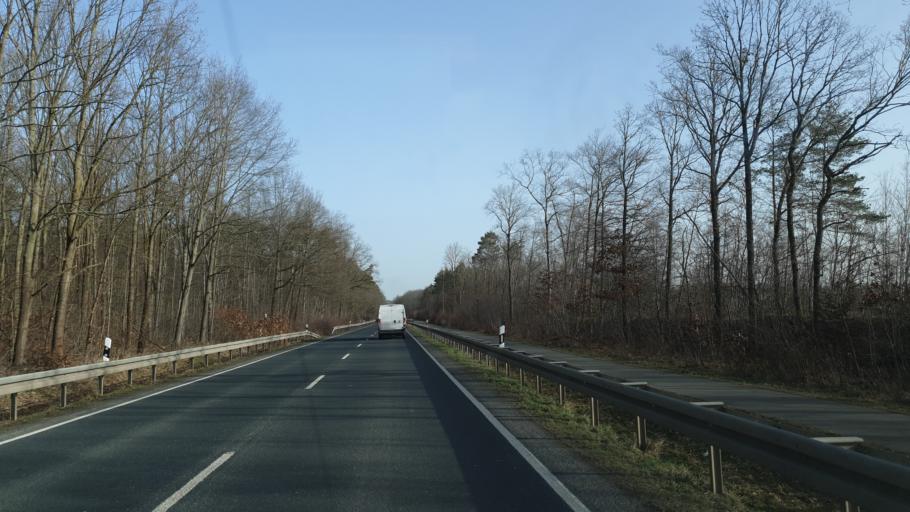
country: DE
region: Saxony
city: Naunhof
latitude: 51.2941
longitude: 12.5925
